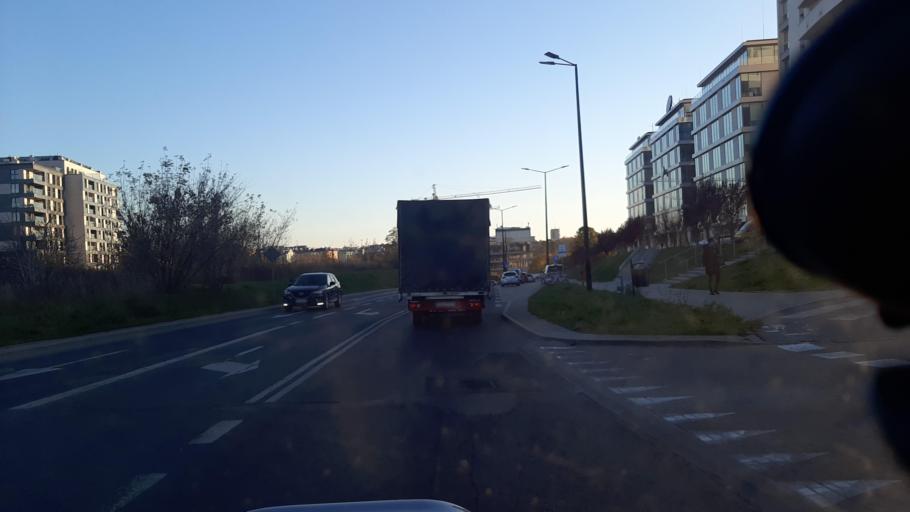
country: PL
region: Lublin Voivodeship
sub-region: Powiat lubelski
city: Lublin
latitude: 51.2571
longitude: 22.5584
